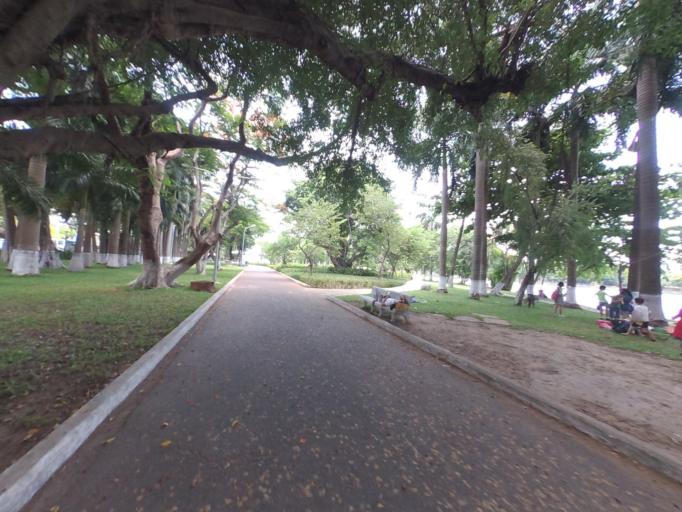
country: VN
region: Da Nang
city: Thanh Khe
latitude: 16.0617
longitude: 108.2049
